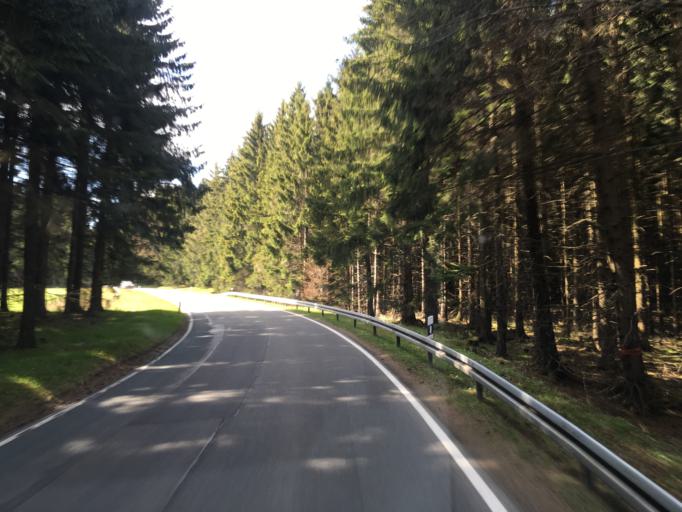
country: DE
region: Lower Saxony
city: Braunlage
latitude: 51.7498
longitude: 10.6873
